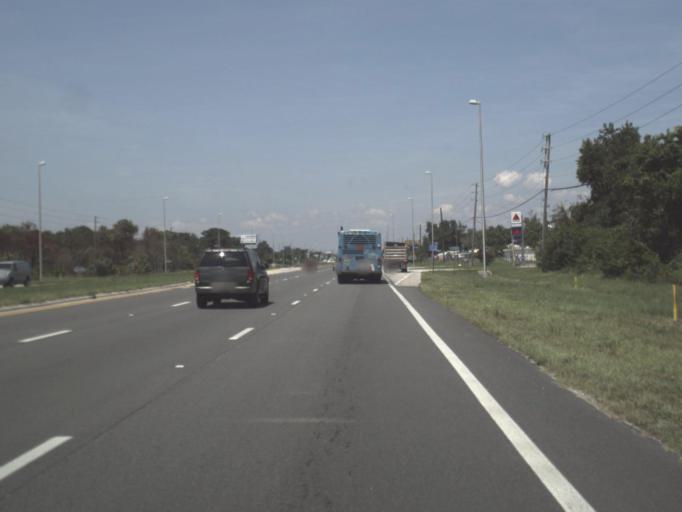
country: US
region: Florida
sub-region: Pasco County
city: Hudson
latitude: 28.3813
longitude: -82.6769
